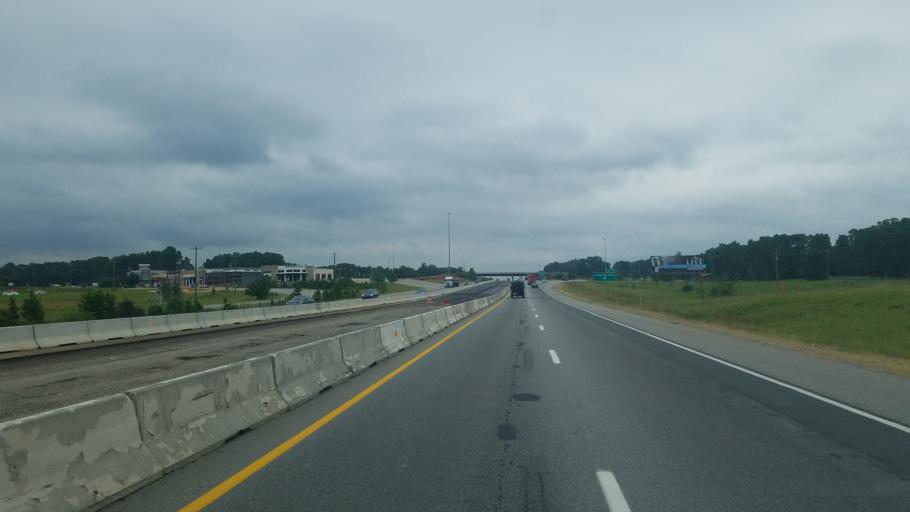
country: US
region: North Carolina
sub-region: Gaston County
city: Davidson
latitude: 35.5246
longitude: -80.8636
